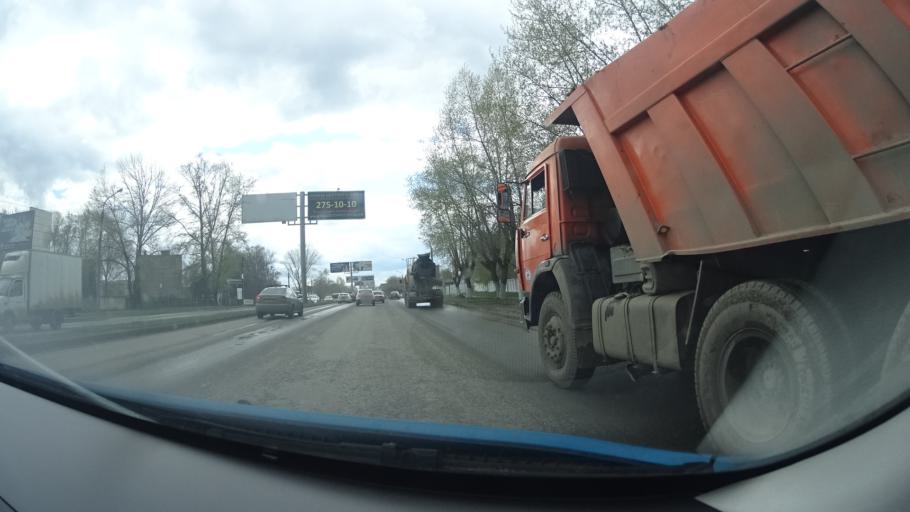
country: RU
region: Bashkortostan
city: Ufa
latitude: 54.8049
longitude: 56.0825
